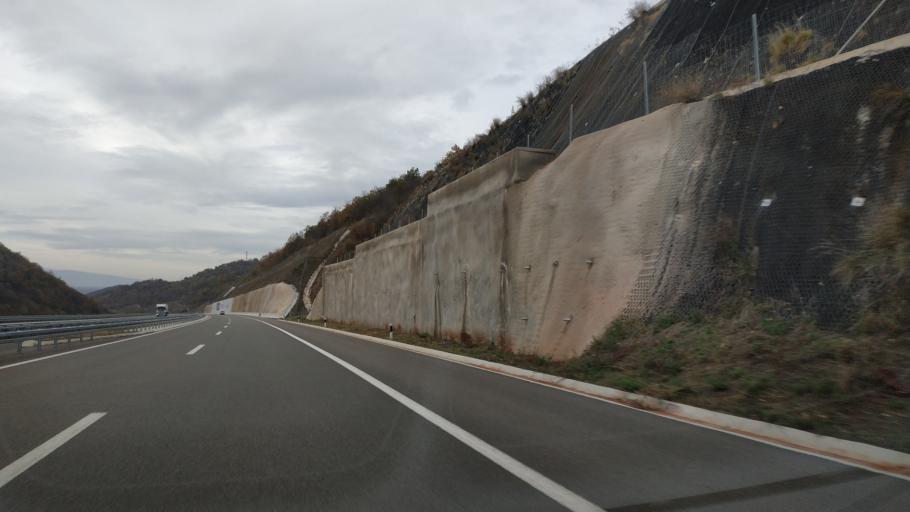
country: RS
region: Central Serbia
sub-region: Nisavski Okrug
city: Niska Banja
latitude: 43.2925
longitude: 22.0995
